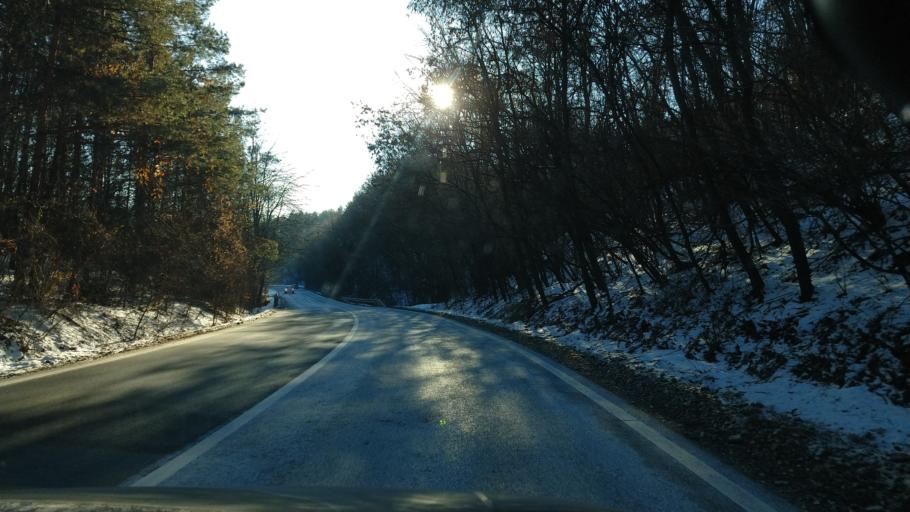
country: RO
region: Bacau
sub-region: Comuna Luizi-Calugara
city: Luizi-Calugara
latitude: 46.5054
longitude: 26.8057
